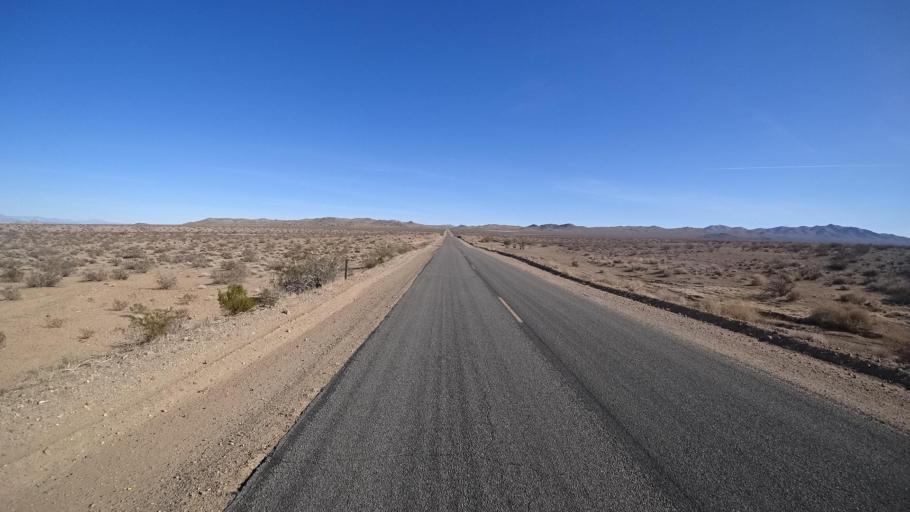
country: US
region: California
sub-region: Kern County
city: China Lake Acres
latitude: 35.5570
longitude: -117.7498
